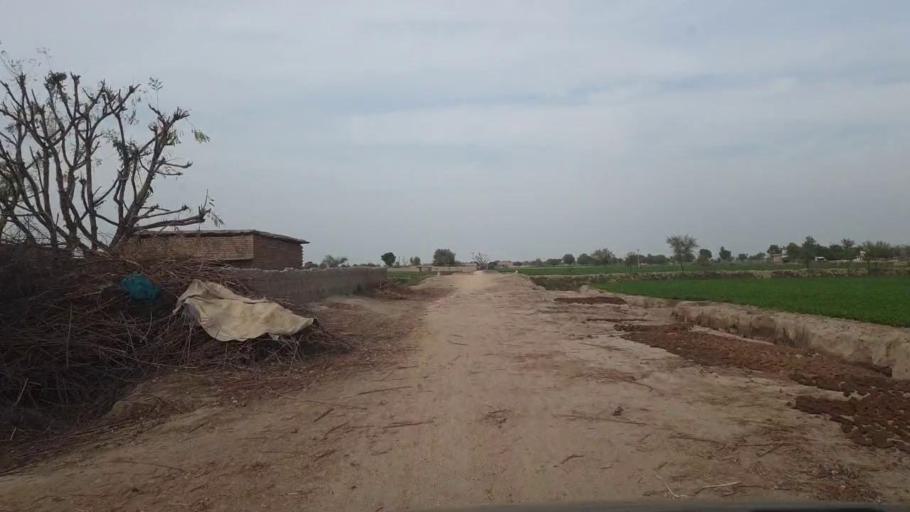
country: PK
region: Sindh
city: Shahpur Chakar
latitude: 26.1189
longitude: 68.5131
